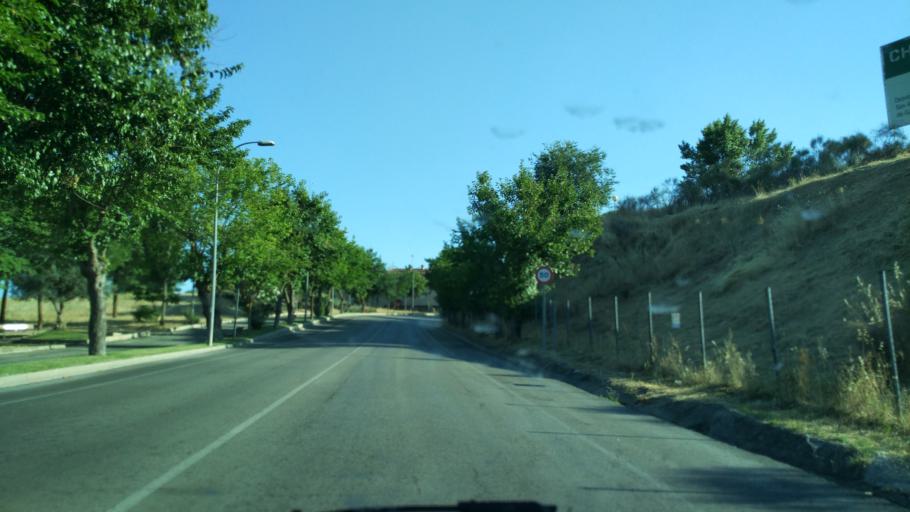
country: ES
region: Madrid
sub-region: Provincia de Madrid
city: San Agustin de Guadalix
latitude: 40.6853
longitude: -3.6111
